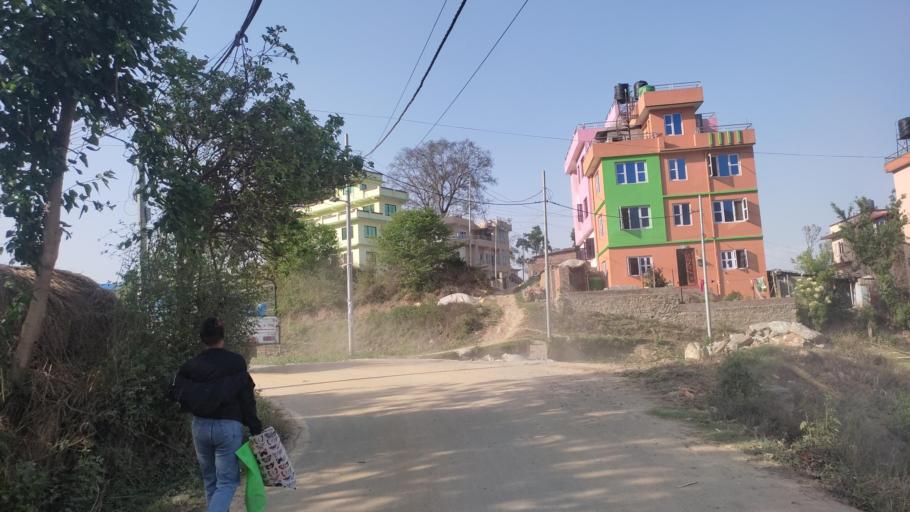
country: NP
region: Central Region
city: Kirtipur
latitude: 27.6527
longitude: 85.2760
